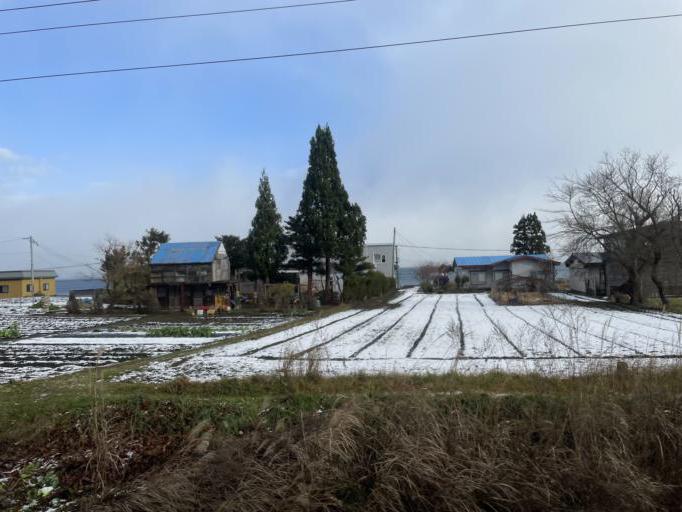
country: JP
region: Aomori
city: Aomori Shi
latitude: 40.9176
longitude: 141.0322
